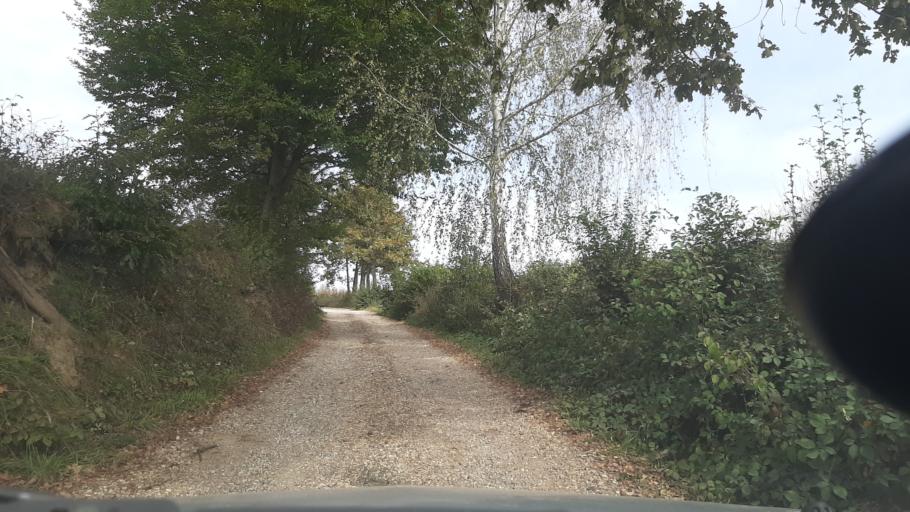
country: BA
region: Republika Srpska
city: Maglajani
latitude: 44.8755
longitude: 17.4725
